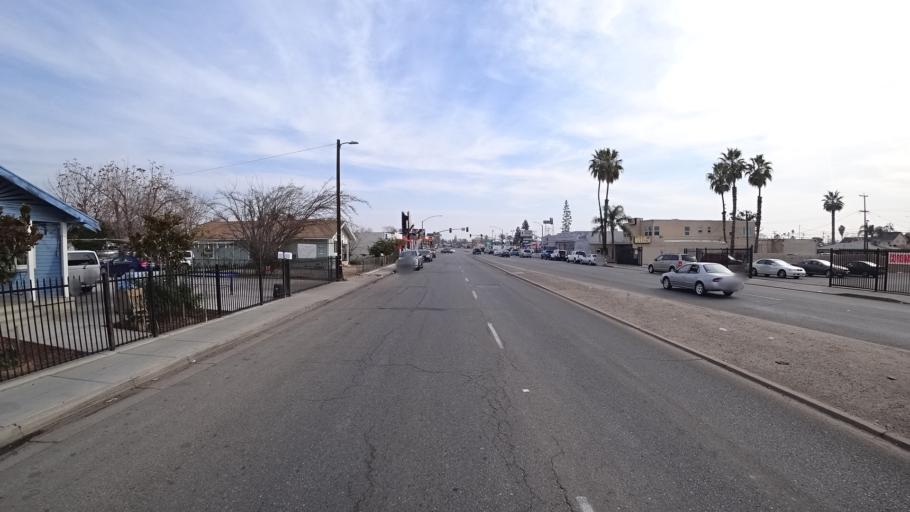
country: US
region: California
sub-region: Kern County
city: Bakersfield
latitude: 35.3767
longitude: -118.9687
